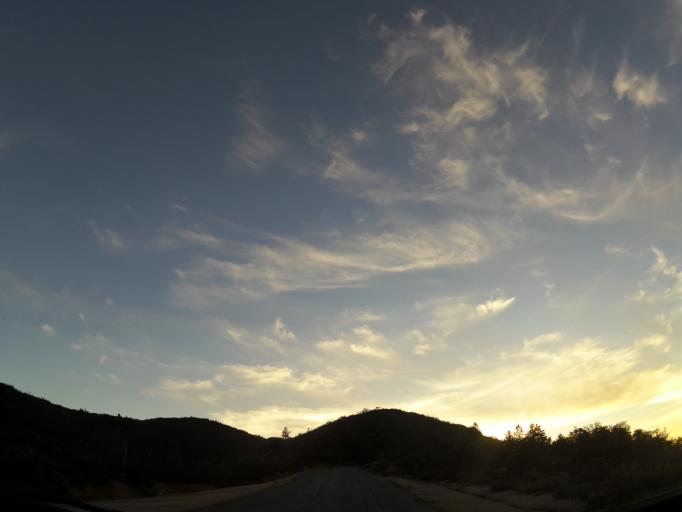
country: US
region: California
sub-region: San Benito County
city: San Juan Bautista
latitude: 36.7788
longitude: -121.4701
